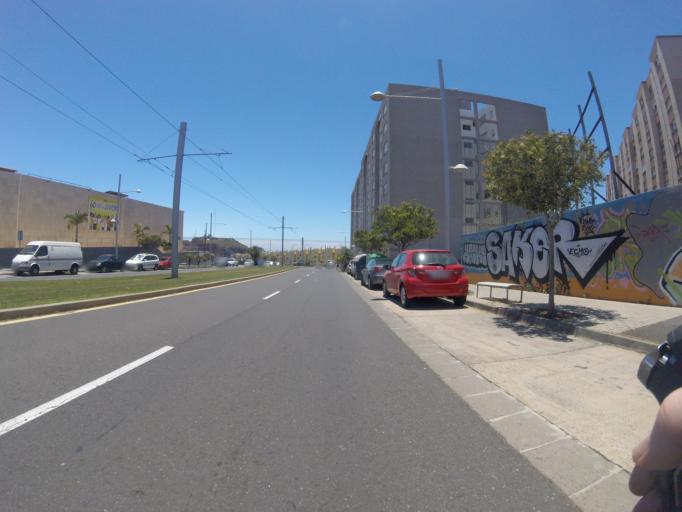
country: ES
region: Canary Islands
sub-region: Provincia de Santa Cruz de Tenerife
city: La Laguna
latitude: 28.4625
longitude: -16.2958
